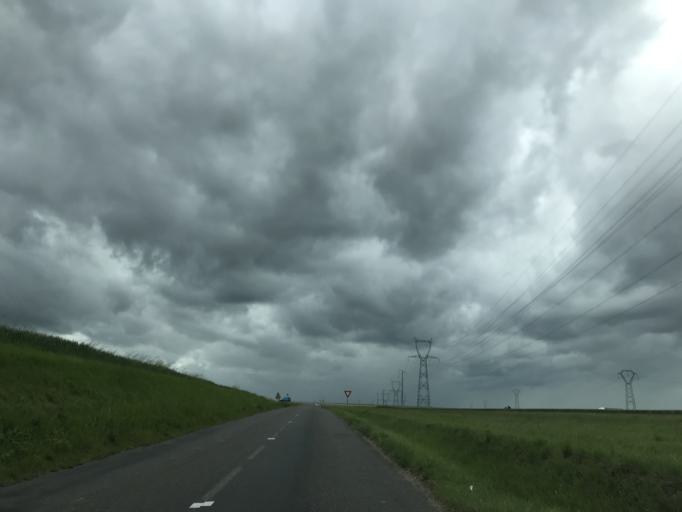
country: FR
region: Haute-Normandie
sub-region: Departement de l'Eure
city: La Couture-Boussey
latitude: 48.8953
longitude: 1.4250
